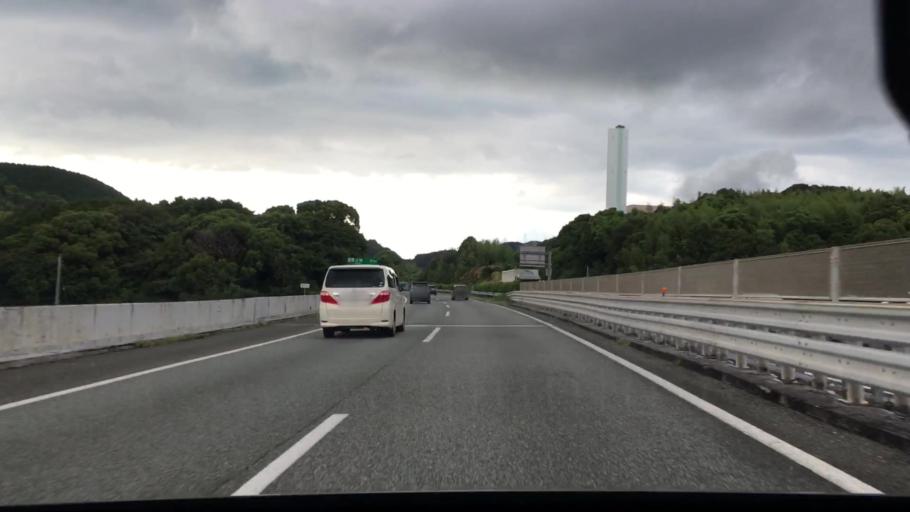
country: JP
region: Fukuoka
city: Sasaguri
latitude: 33.6390
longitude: 130.4892
